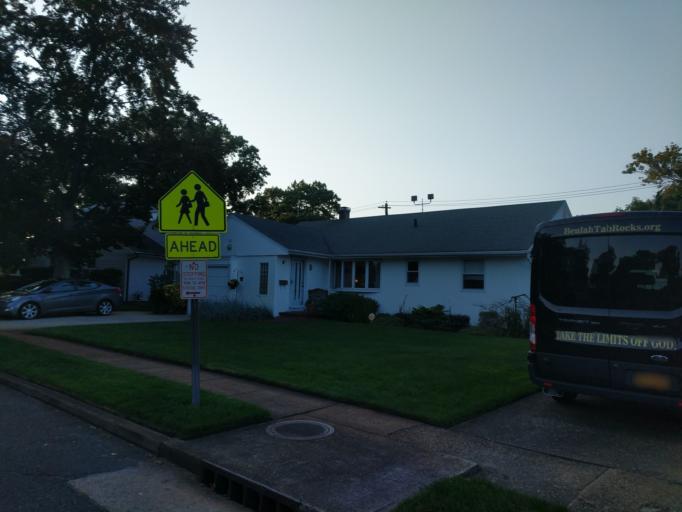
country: US
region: New York
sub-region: Nassau County
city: South Valley Stream
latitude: 40.6532
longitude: -73.7121
